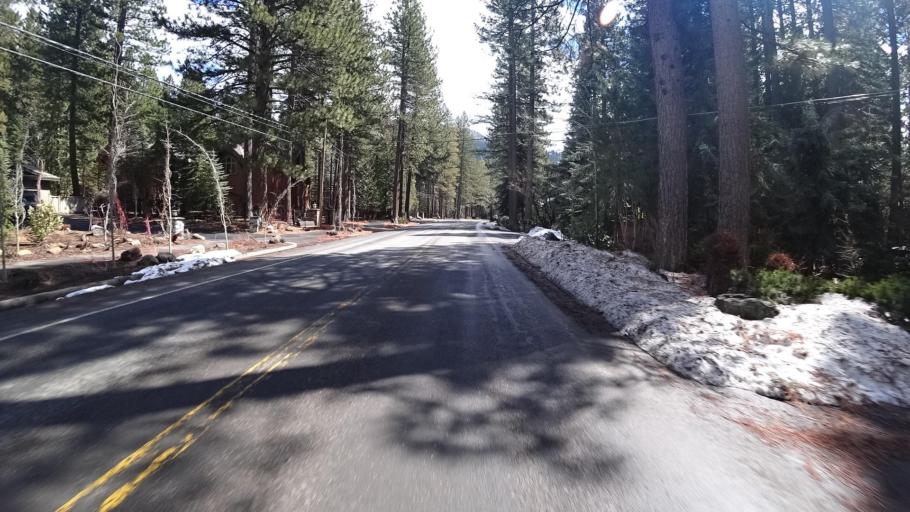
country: US
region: Nevada
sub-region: Washoe County
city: Incline Village
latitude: 39.2380
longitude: -119.9383
